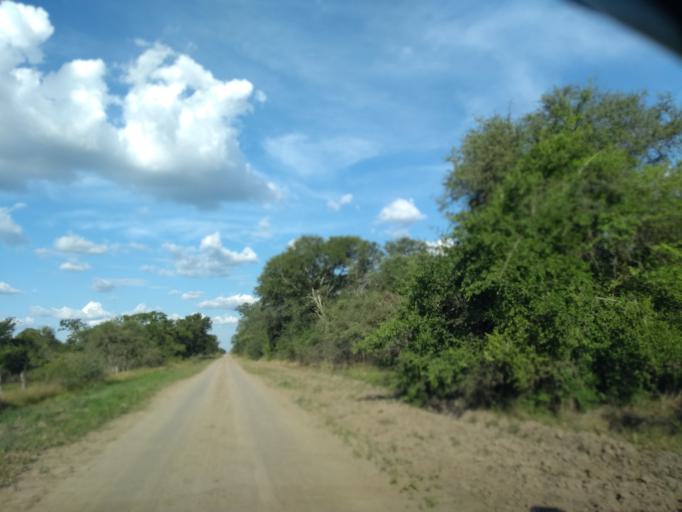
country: AR
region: Chaco
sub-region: Departamento de Quitilipi
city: Quitilipi
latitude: -26.7622
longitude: -60.2285
